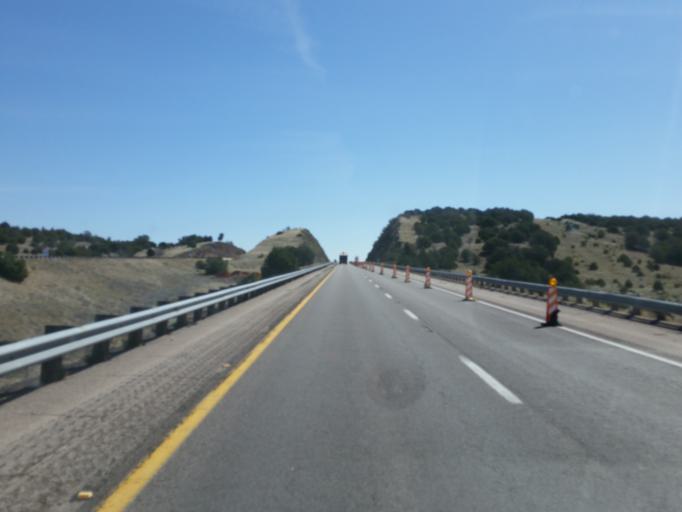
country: US
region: Arizona
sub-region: Mohave County
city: Peach Springs
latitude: 35.2378
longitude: -113.2047
